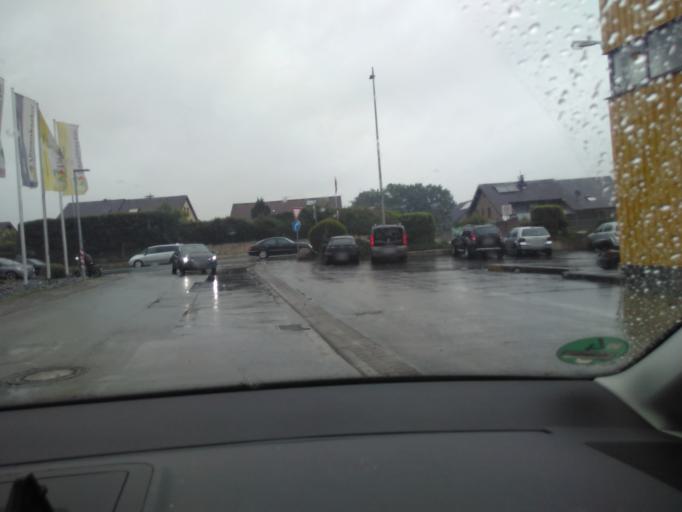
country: DE
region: North Rhine-Westphalia
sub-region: Regierungsbezirk Detmold
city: Bielefeld
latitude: 52.0388
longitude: 8.5957
